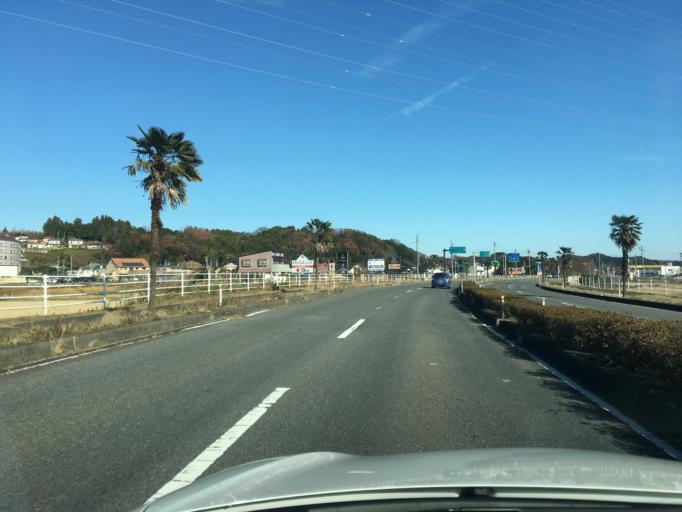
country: JP
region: Fukushima
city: Iwaki
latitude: 36.9835
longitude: 140.8429
